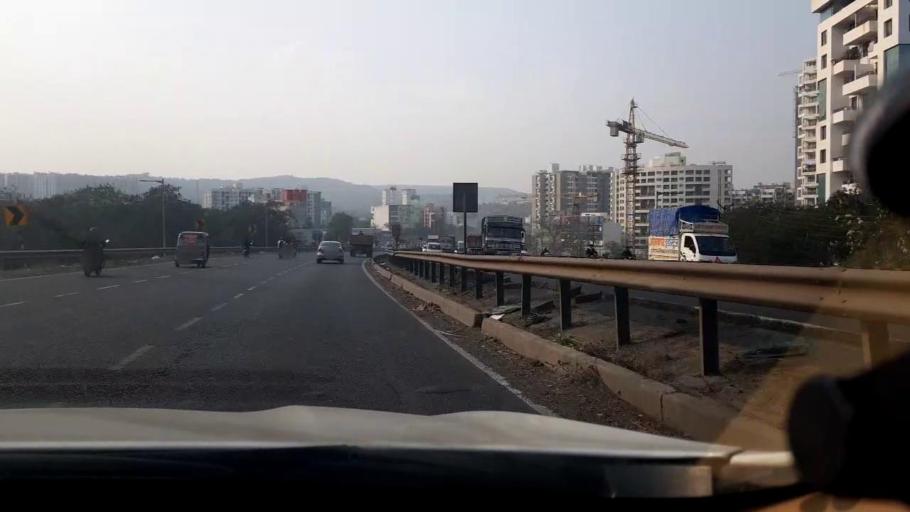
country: IN
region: Maharashtra
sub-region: Pune Division
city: Kharakvasla
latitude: 18.5094
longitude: 73.7744
